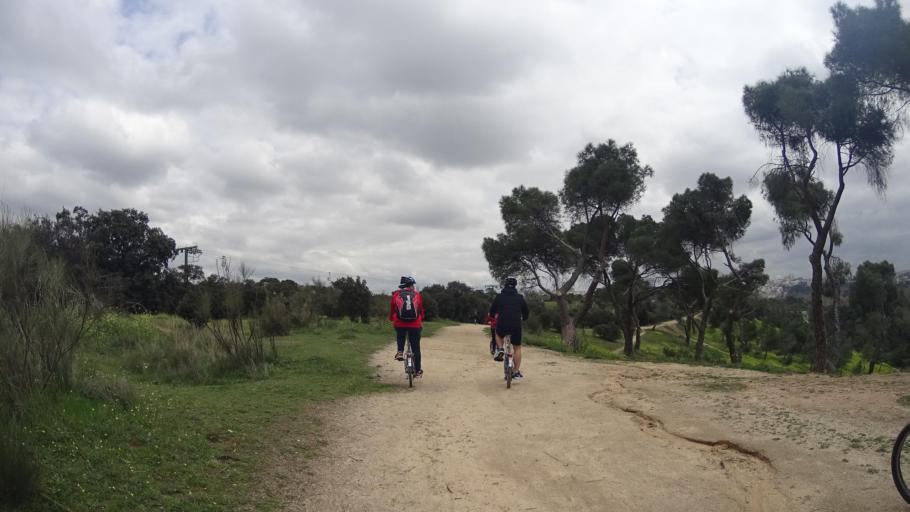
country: ES
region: Madrid
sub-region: Provincia de Madrid
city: Moncloa-Aravaca
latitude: 40.4195
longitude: -3.7452
